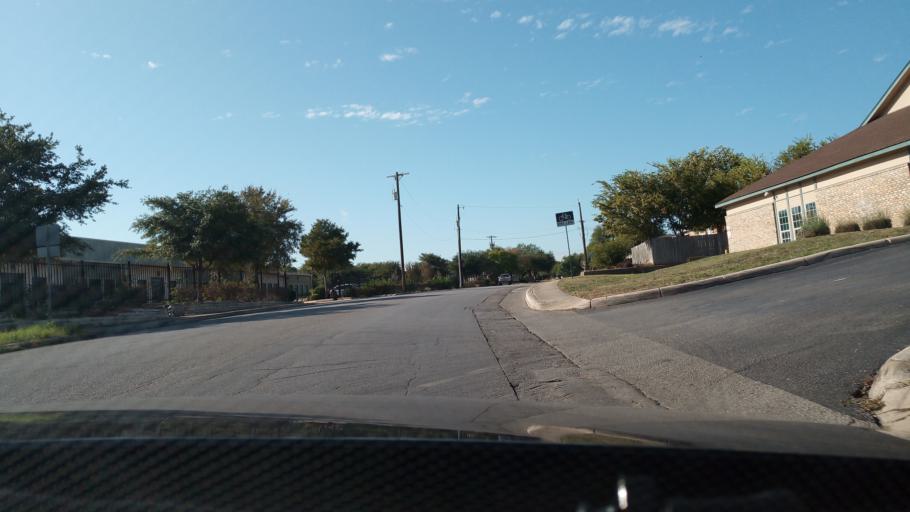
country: US
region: Texas
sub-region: Bexar County
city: Windcrest
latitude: 29.5531
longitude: -98.4296
